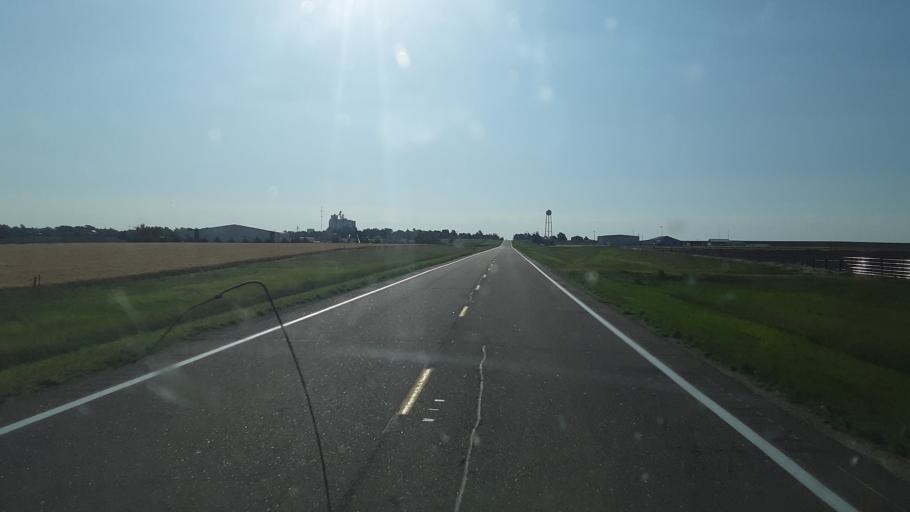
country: US
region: Kansas
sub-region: Edwards County
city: Kinsley
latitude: 38.1897
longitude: -99.5402
